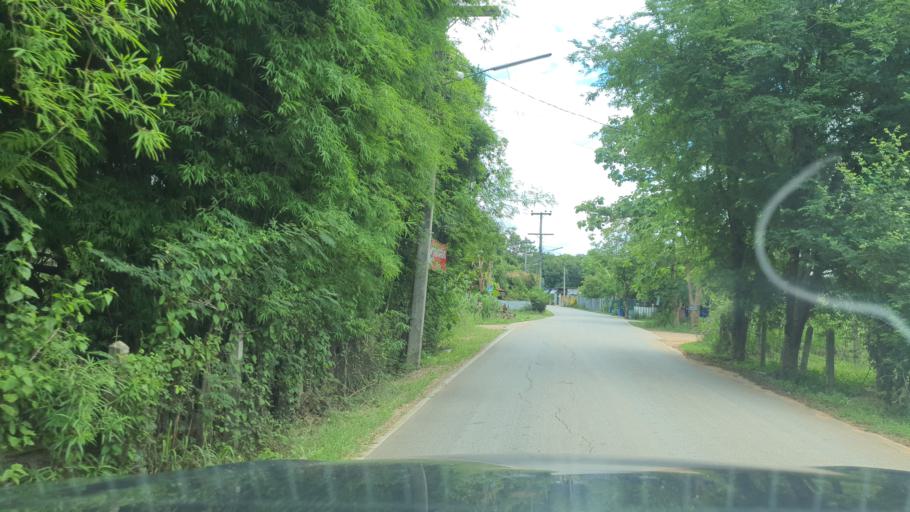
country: TH
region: Chiang Mai
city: San Sai
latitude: 18.9118
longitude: 99.0462
